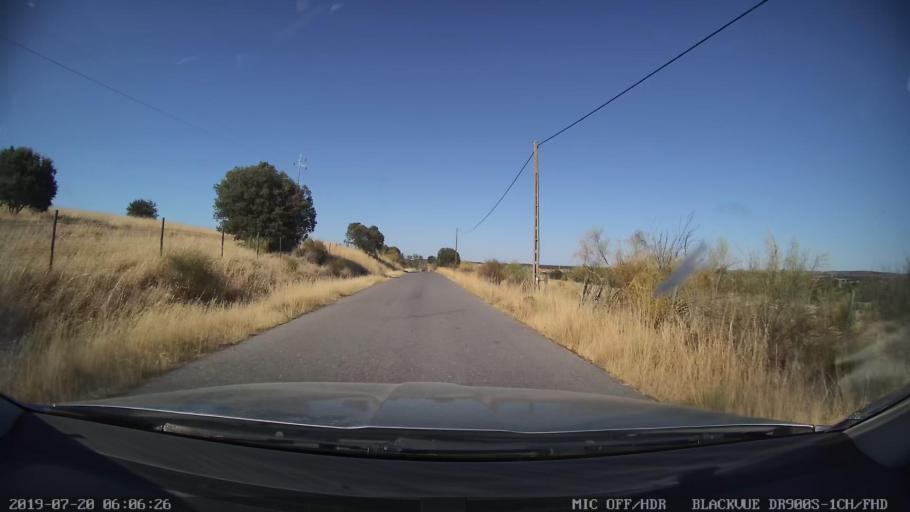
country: PT
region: Castelo Branco
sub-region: Idanha-A-Nova
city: Idanha-a-Nova
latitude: 39.8696
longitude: -7.1495
